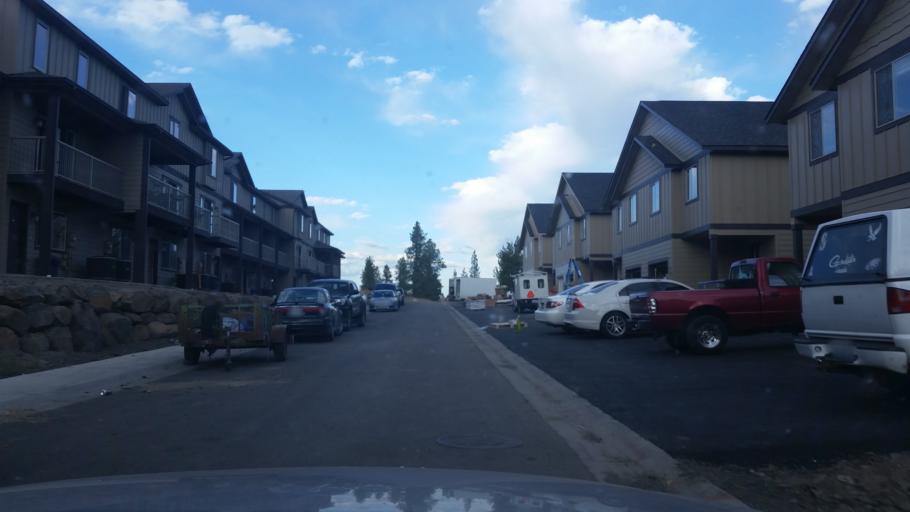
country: US
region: Washington
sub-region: Spokane County
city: Cheney
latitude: 47.4820
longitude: -117.5772
